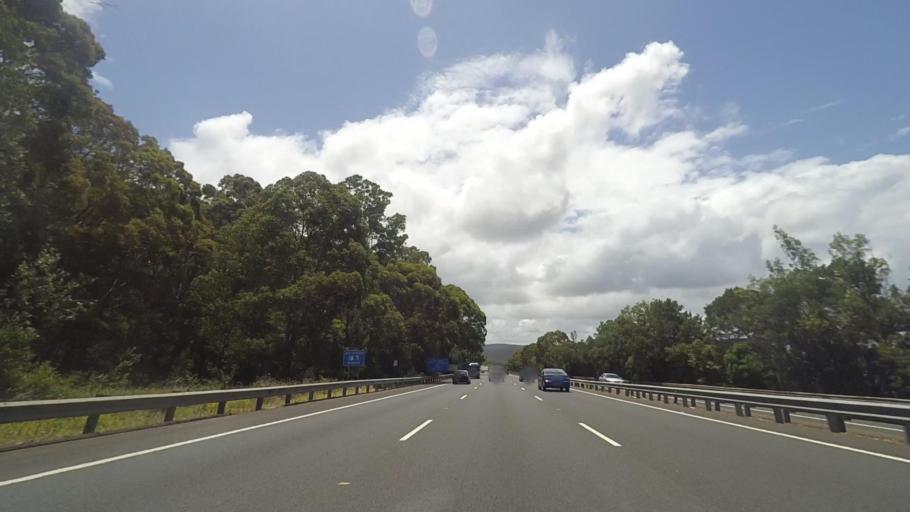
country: AU
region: New South Wales
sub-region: Hornsby Shire
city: Berowra
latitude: -33.5449
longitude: 151.1970
